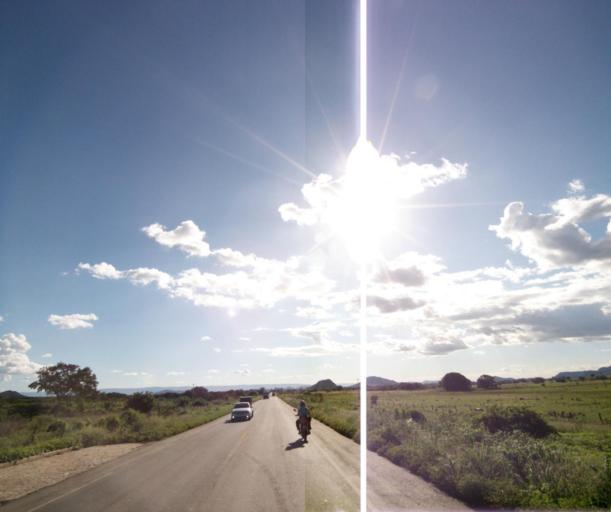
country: BR
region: Bahia
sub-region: Guanambi
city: Guanambi
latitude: -14.1579
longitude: -42.7087
